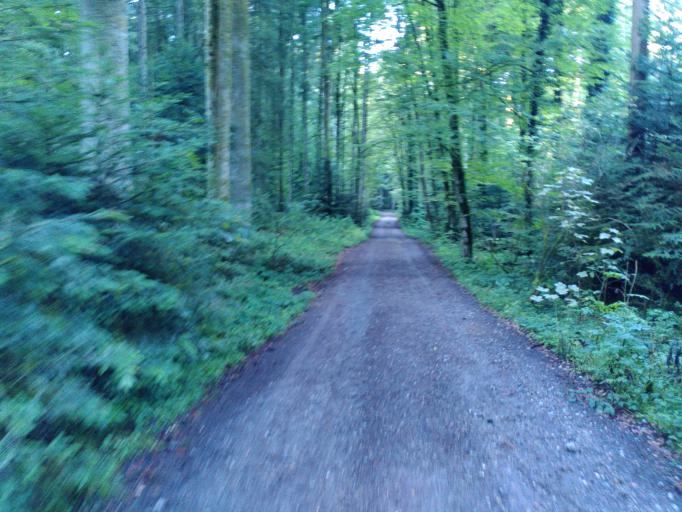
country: CH
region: Bern
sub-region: Emmental District
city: Ersigen
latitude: 47.0965
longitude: 7.6206
